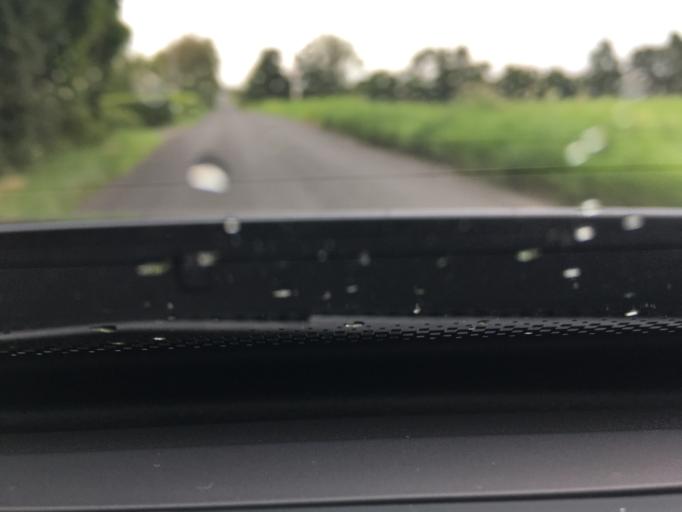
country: GB
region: Northern Ireland
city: Coalisland
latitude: 54.5187
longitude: -6.6296
